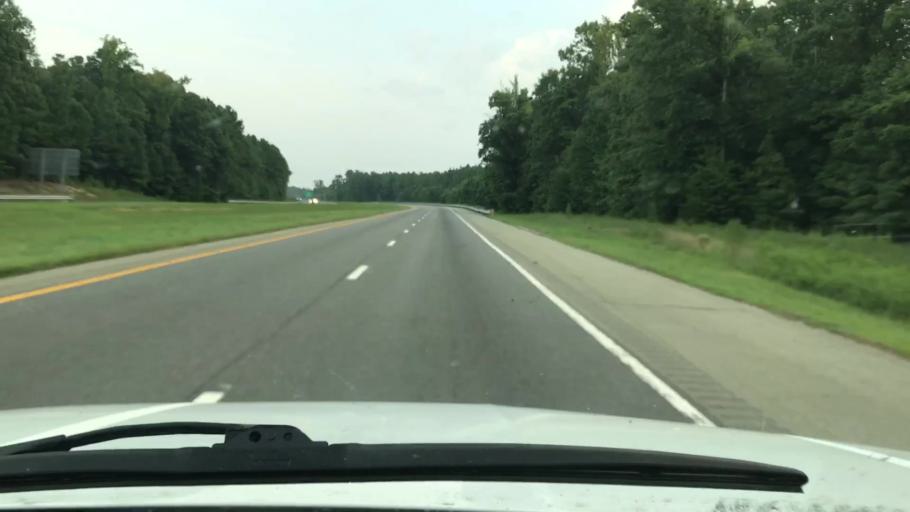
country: US
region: Virginia
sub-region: Chesterfield County
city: Brandermill
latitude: 37.5417
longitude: -77.6945
